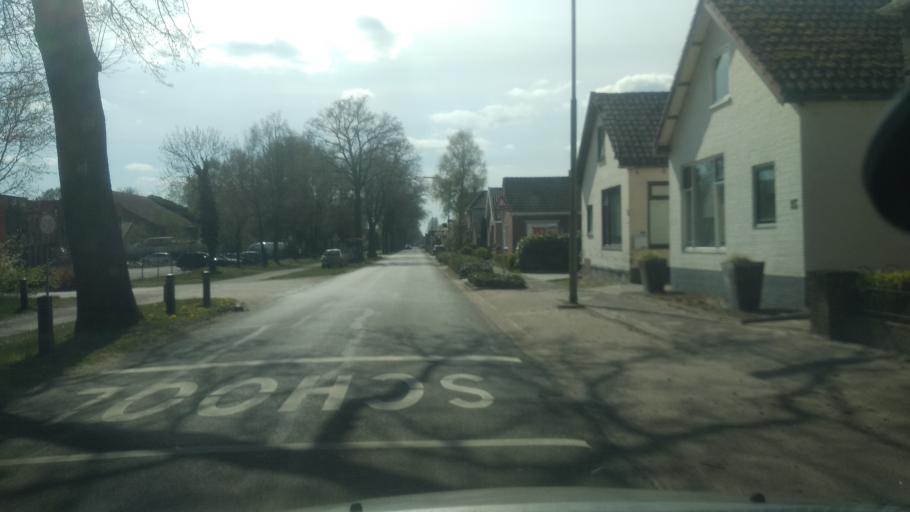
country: NL
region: Groningen
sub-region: Gemeente Stadskanaal
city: Stadskanaal
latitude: 52.9433
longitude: 6.9021
